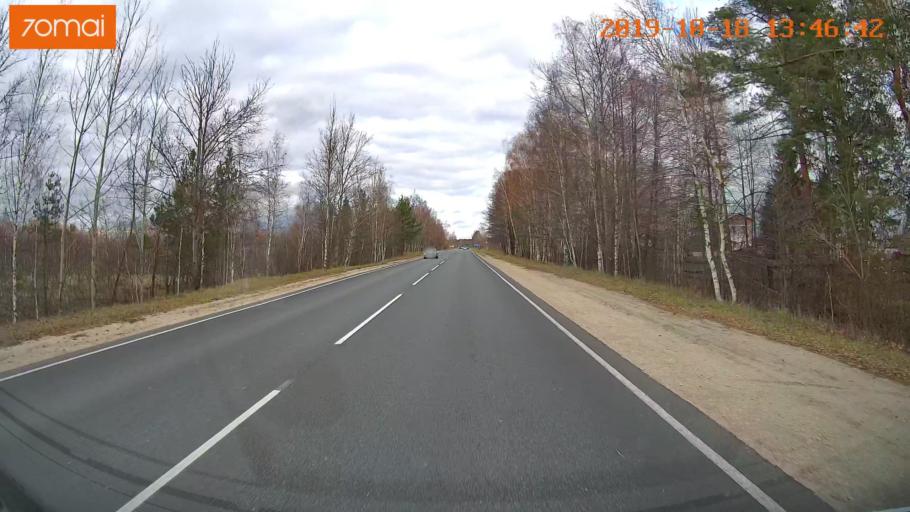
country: RU
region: Rjazan
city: Solotcha
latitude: 54.9645
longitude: 39.9457
